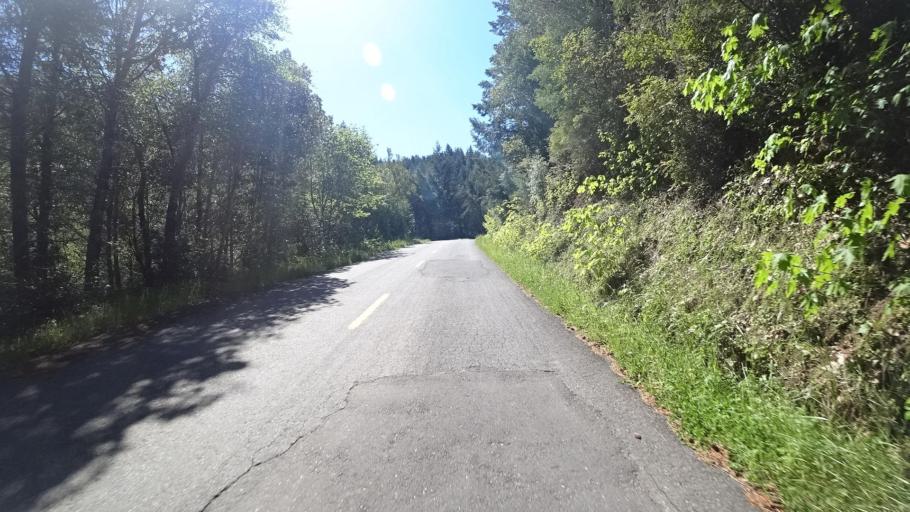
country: US
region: California
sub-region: Humboldt County
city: Rio Dell
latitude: 40.2281
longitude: -124.1101
